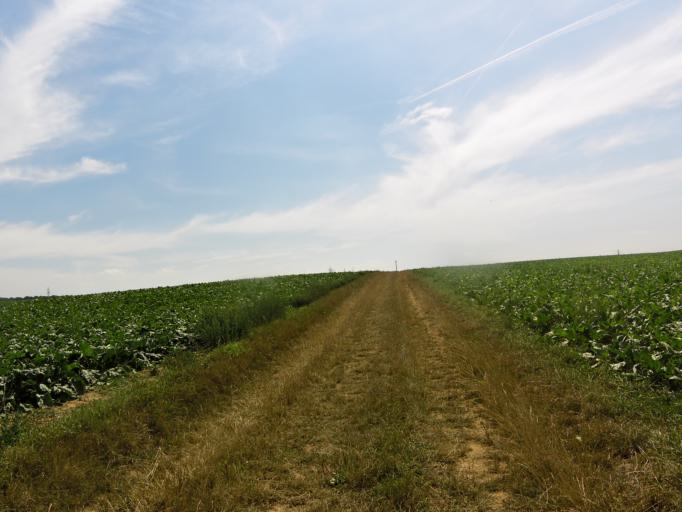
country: DE
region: Bavaria
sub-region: Regierungsbezirk Unterfranken
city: Estenfeld
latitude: 49.8073
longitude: 10.0057
